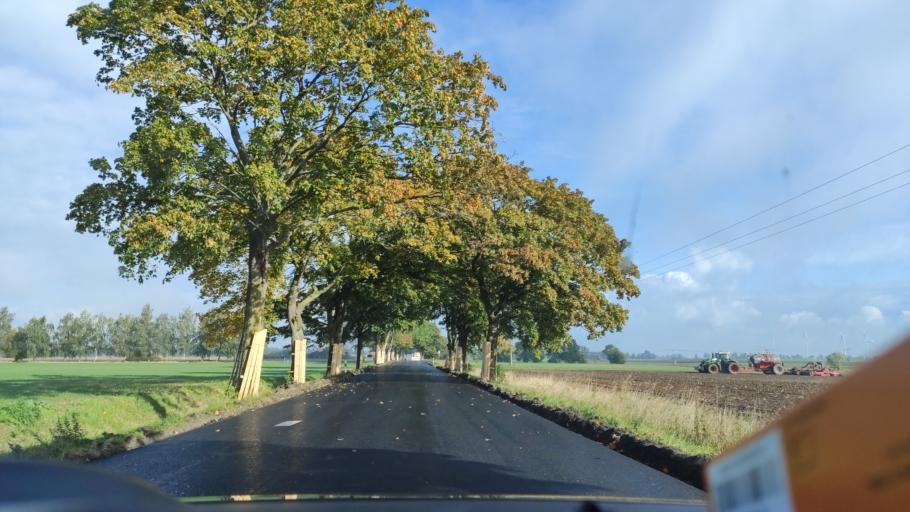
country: DE
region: Mecklenburg-Vorpommern
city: Dersekow
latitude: 54.0628
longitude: 13.1786
